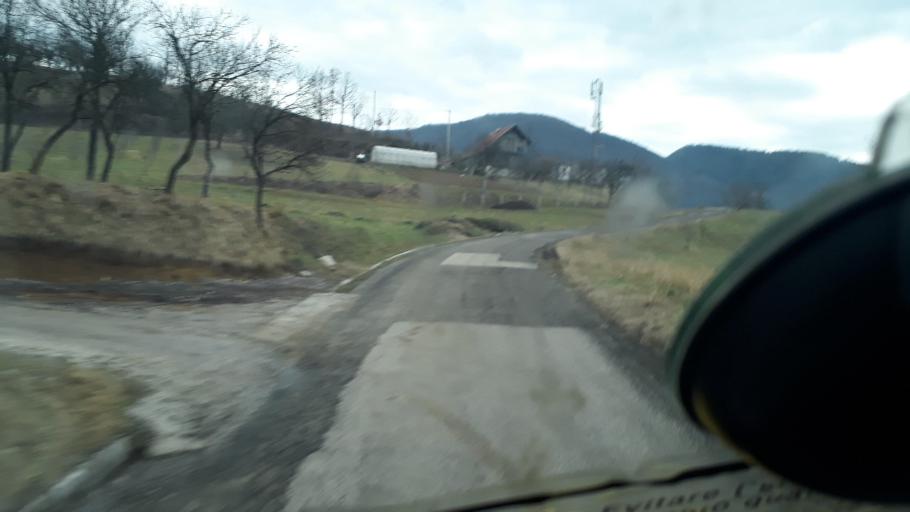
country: BA
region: Federation of Bosnia and Herzegovina
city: Zenica
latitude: 44.1578
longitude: 17.9686
